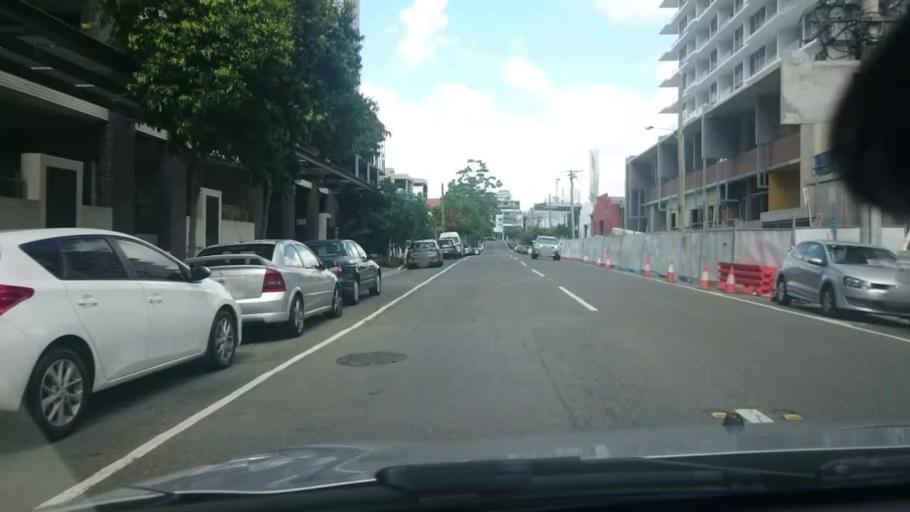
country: AU
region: Queensland
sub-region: Brisbane
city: Fortitude Valley
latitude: -27.4518
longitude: 153.0464
